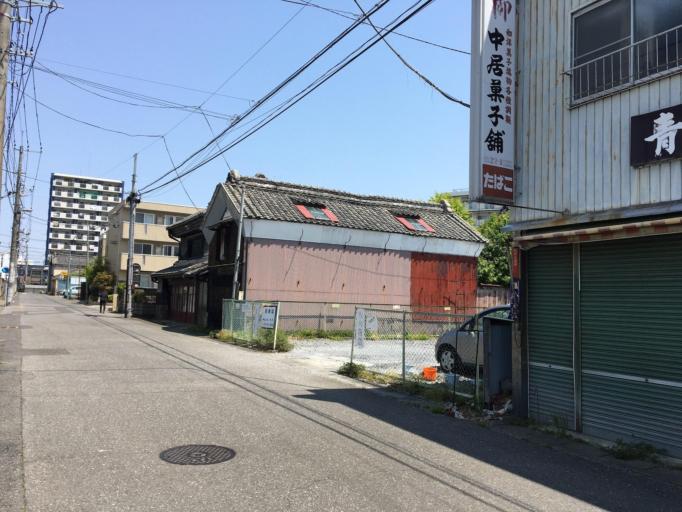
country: JP
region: Ibaraki
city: Koga
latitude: 36.1935
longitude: 139.7041
